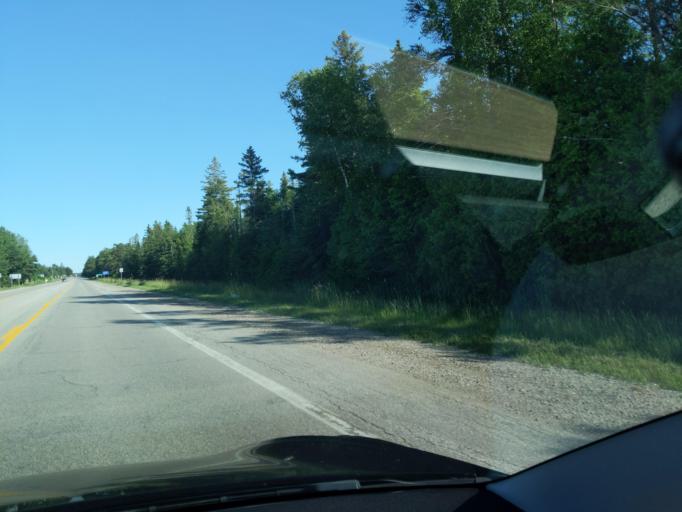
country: US
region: Michigan
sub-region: Mackinac County
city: Saint Ignace
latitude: 45.7633
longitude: -84.7159
